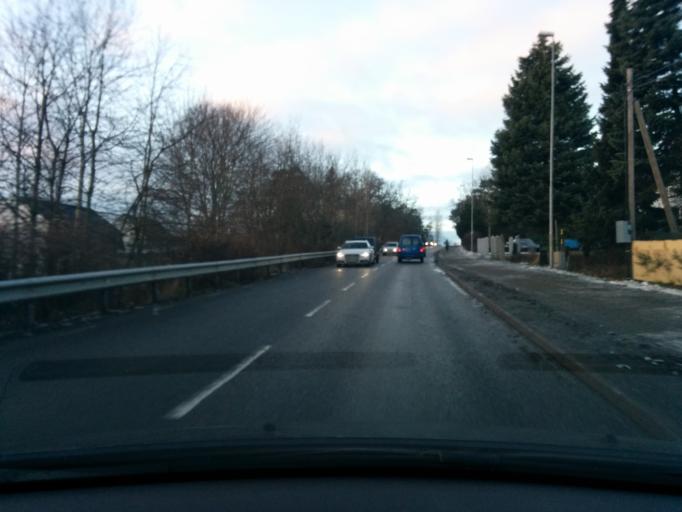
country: SE
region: Stockholm
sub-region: Nacka Kommun
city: Alta
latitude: 59.2640
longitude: 18.1796
